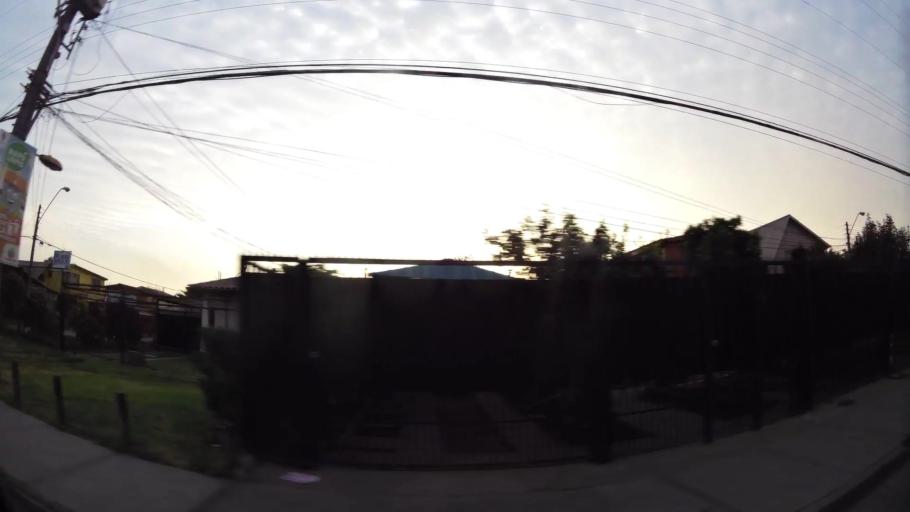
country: CL
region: Santiago Metropolitan
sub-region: Provincia de Santiago
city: Lo Prado
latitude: -33.5178
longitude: -70.7792
